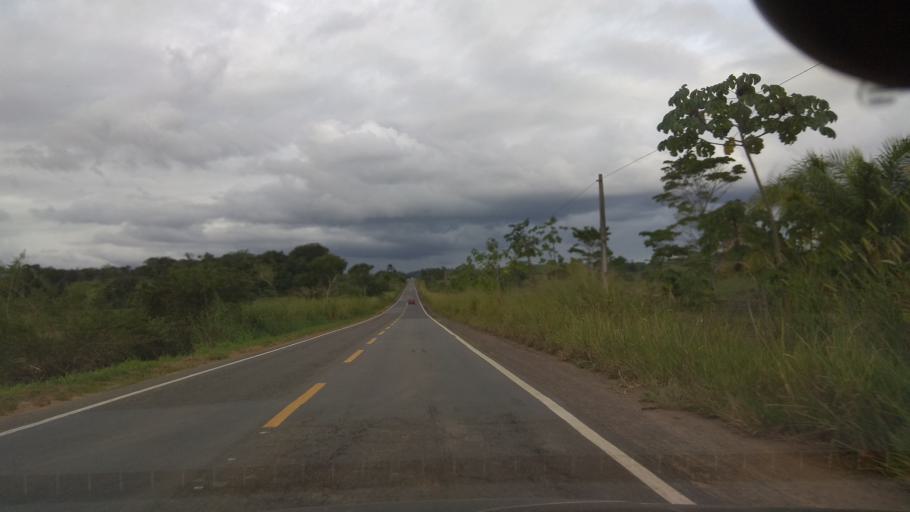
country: BR
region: Bahia
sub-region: Ubata
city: Ubata
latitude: -14.1952
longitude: -39.6360
